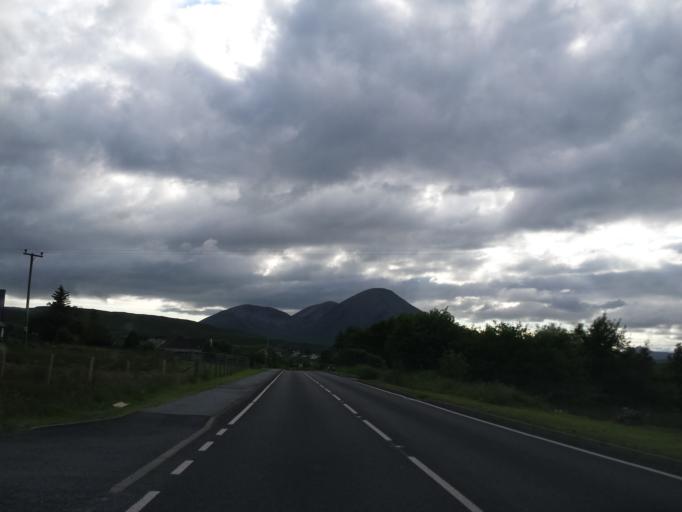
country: GB
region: Scotland
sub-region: Highland
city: Portree
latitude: 57.2369
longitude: -5.8762
